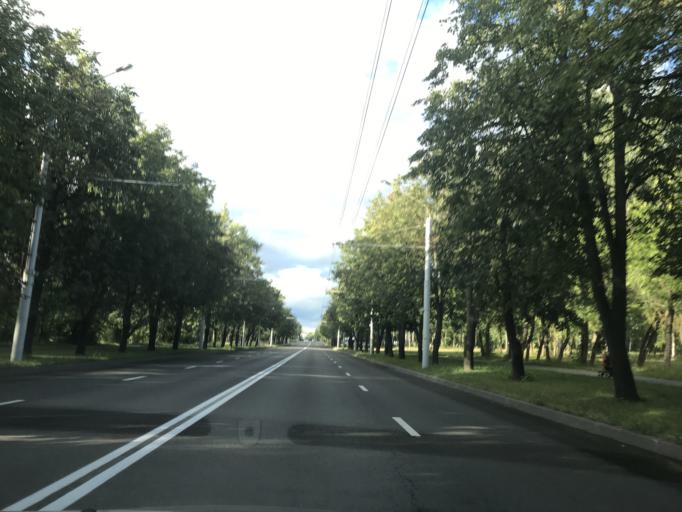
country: BY
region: Minsk
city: Minsk
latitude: 53.9417
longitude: 27.6188
